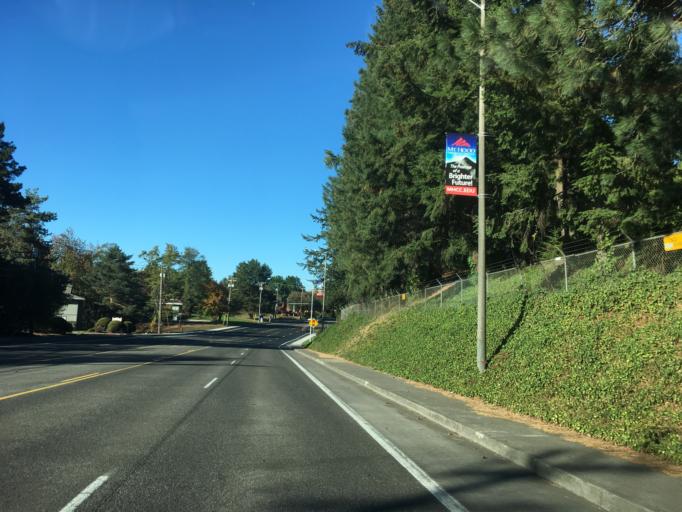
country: US
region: Oregon
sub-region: Multnomah County
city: Wood Village
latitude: 45.5109
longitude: -122.3999
